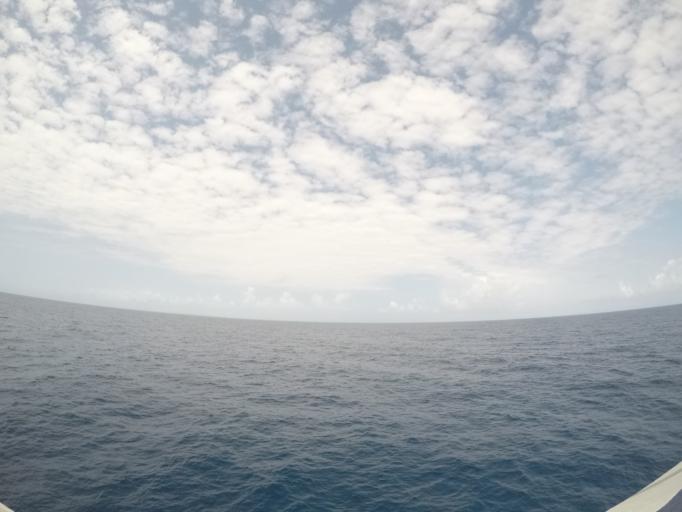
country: TZ
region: Zanzibar North
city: Nungwi
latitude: -5.5893
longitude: 39.3506
